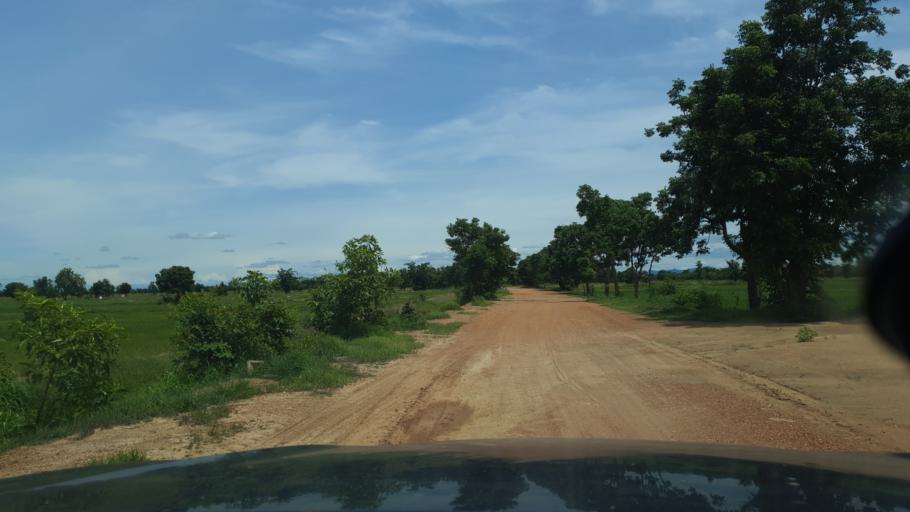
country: TH
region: Sukhothai
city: Ban Na
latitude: 17.0689
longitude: 99.7033
